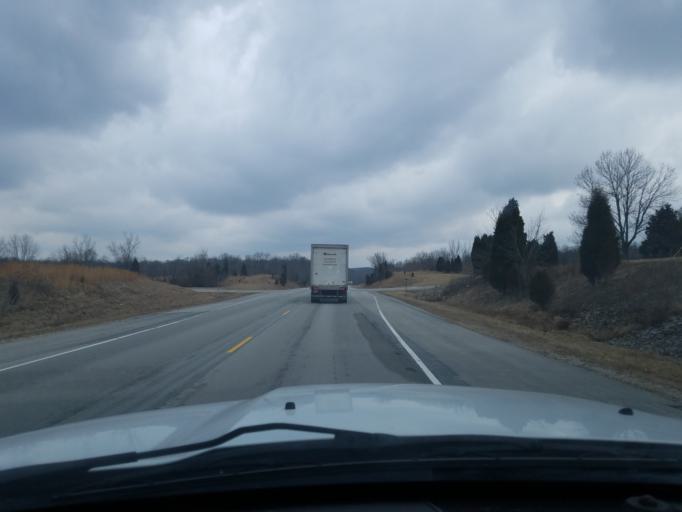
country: US
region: Indiana
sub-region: Crawford County
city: English
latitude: 38.1736
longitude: -86.6044
